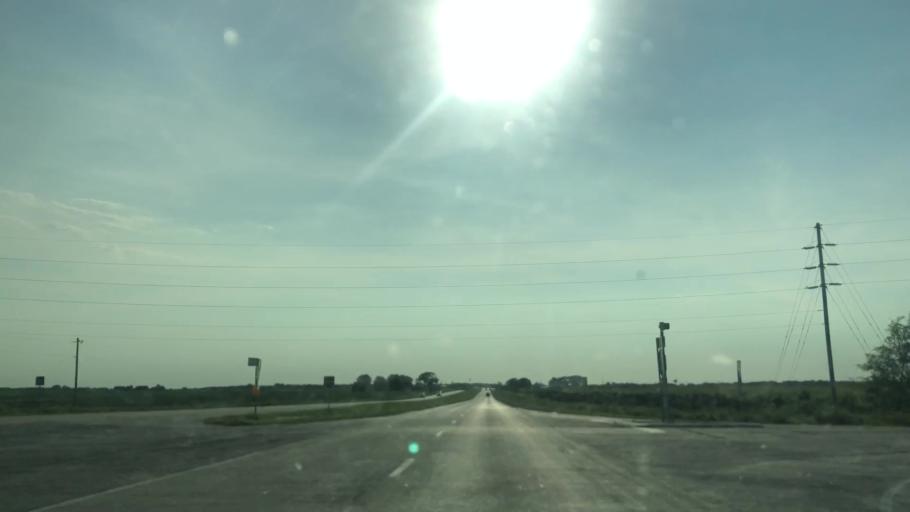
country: US
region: Iowa
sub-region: Story County
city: Nevada
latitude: 42.0080
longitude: -93.4054
